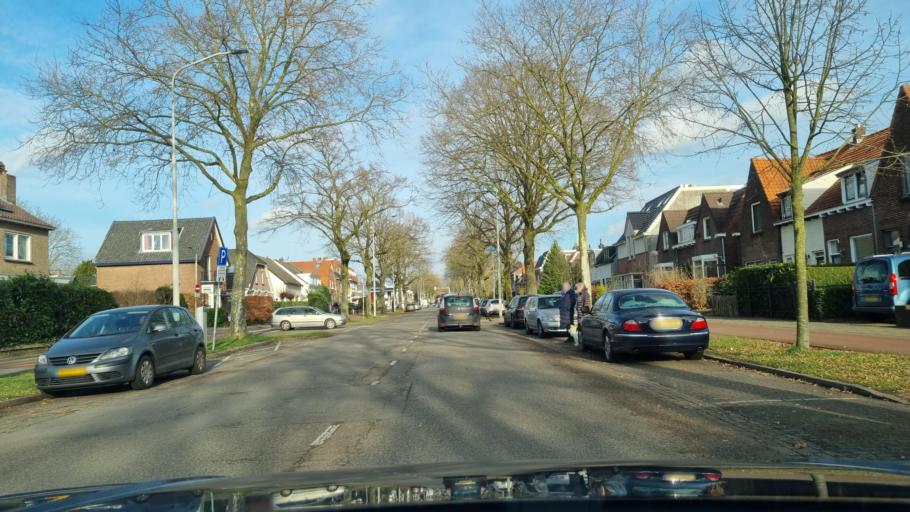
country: NL
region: Gelderland
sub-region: Gemeente Nijmegen
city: Nijmegen
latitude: 51.8219
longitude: 5.8489
